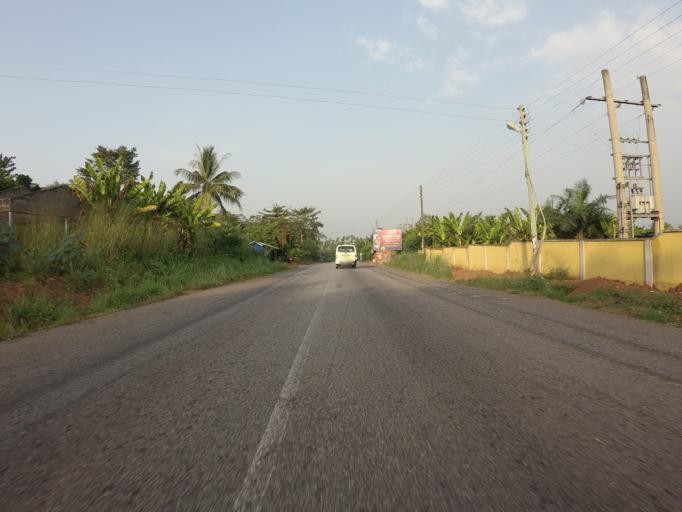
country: GH
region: Volta
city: Ho
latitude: 6.5311
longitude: 0.2799
